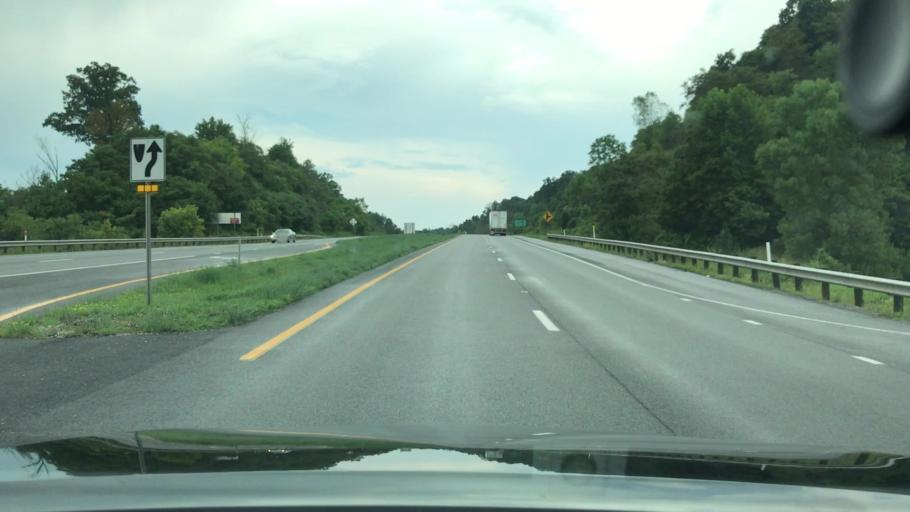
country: US
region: West Virginia
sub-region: Mason County
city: Point Pleasant
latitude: 38.8266
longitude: -82.1292
